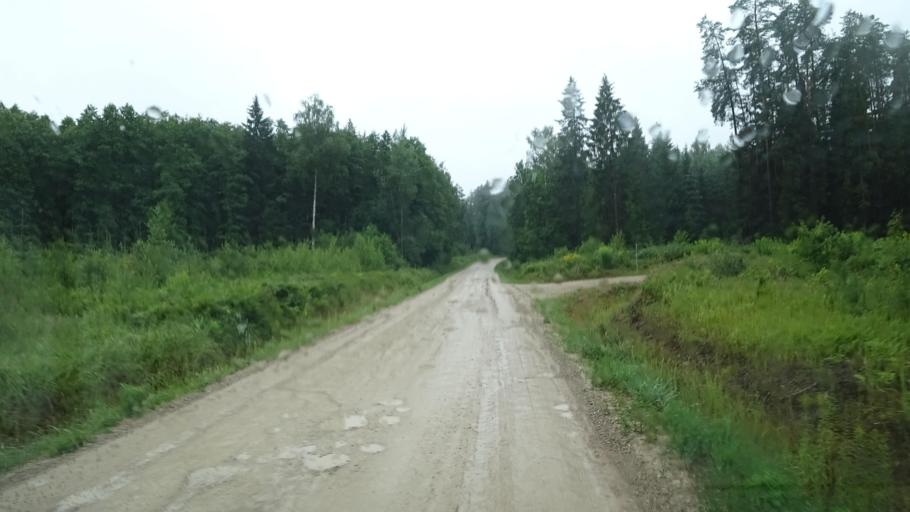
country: LV
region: Lecava
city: Iecava
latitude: 56.6527
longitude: 24.1743
